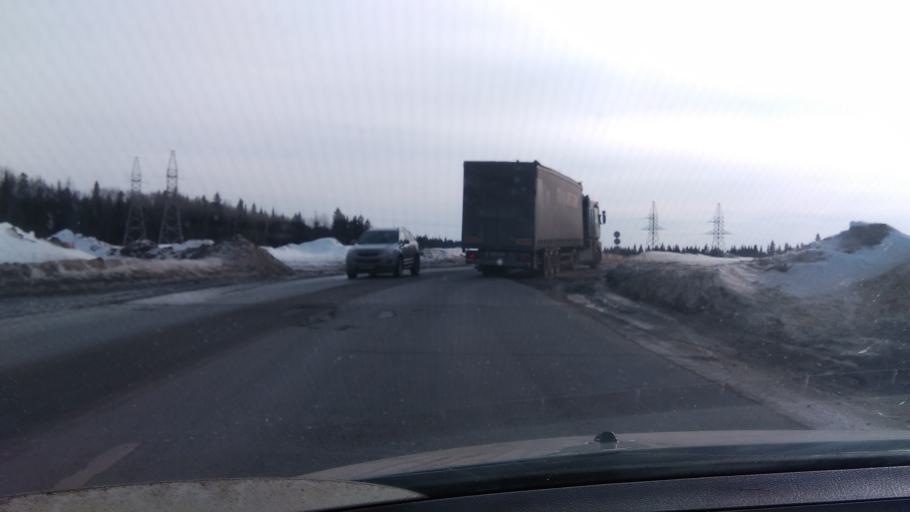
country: RU
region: Perm
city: Ferma
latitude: 57.9523
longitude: 56.3913
